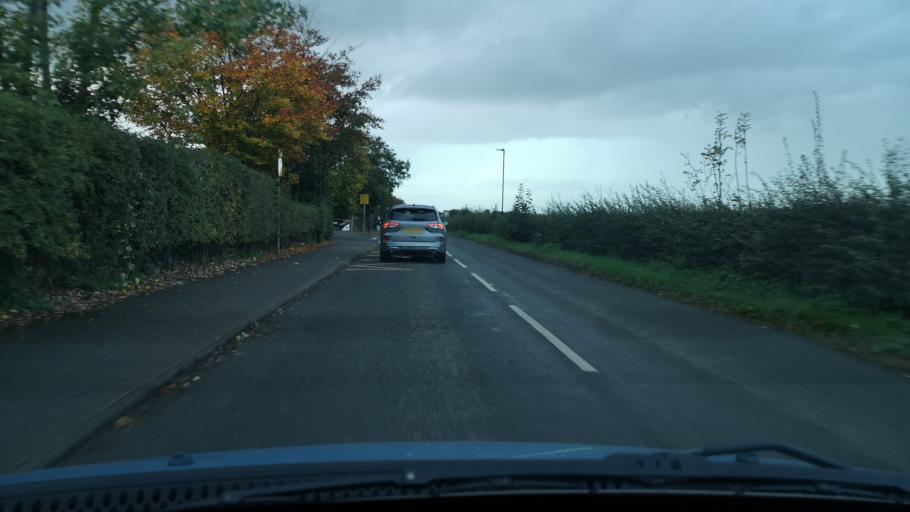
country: GB
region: England
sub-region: Doncaster
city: Campsall
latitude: 53.6248
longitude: -1.1807
